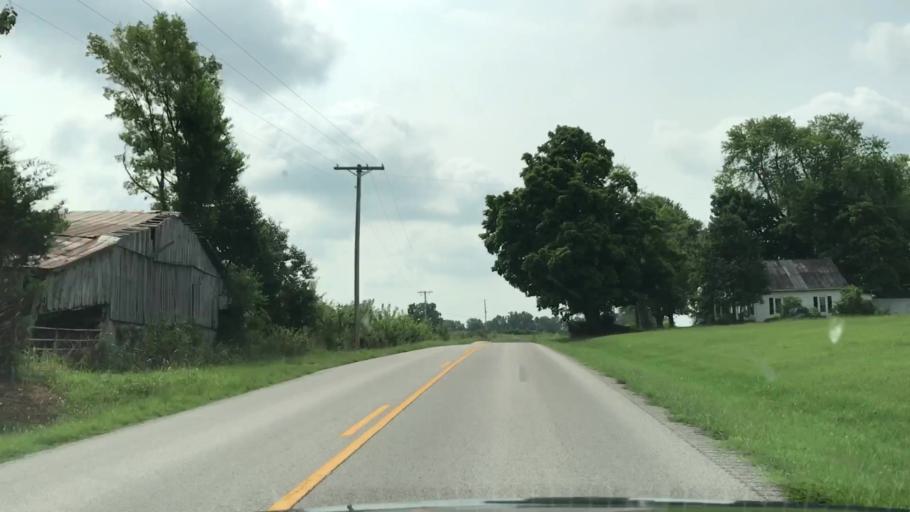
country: US
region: Kentucky
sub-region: Edmonson County
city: Brownsville
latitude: 37.1086
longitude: -86.1469
